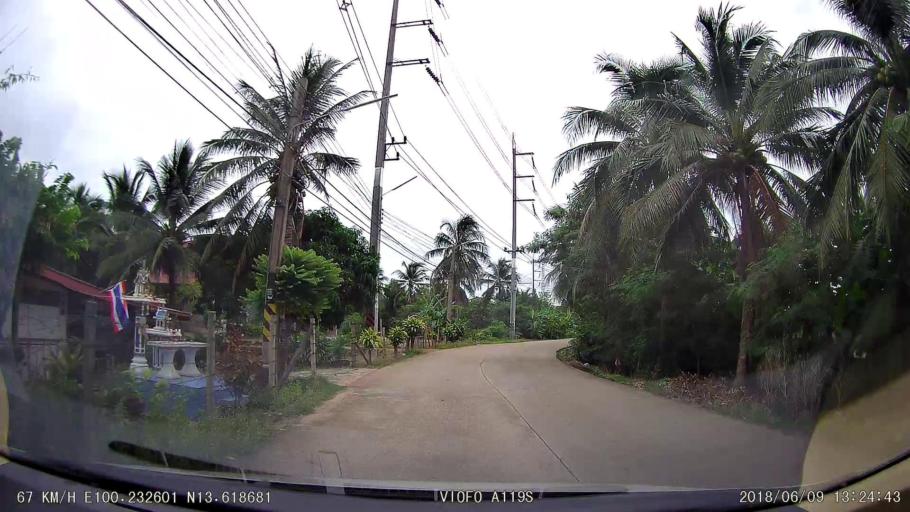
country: TH
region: Samut Sakhon
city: Krathum Baen
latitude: 13.6188
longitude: 100.2326
